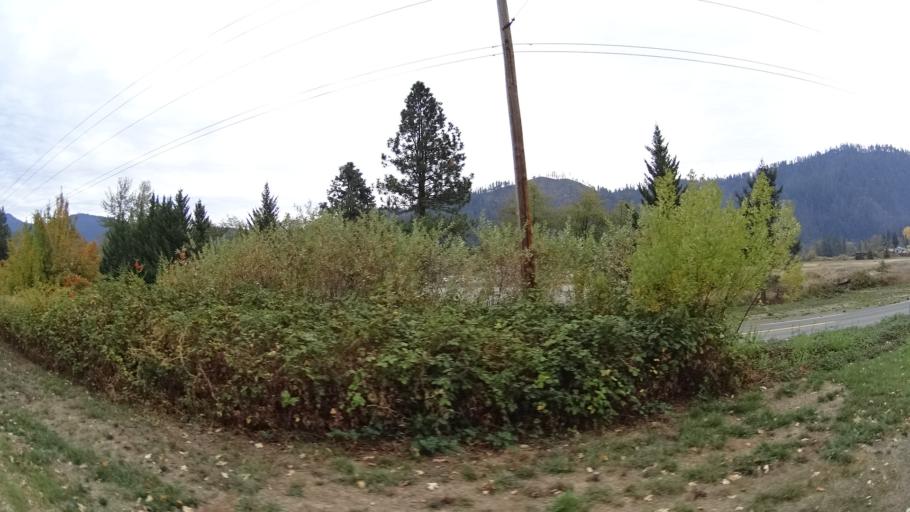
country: US
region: California
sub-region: Siskiyou County
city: Happy Camp
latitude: 41.8038
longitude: -123.3720
